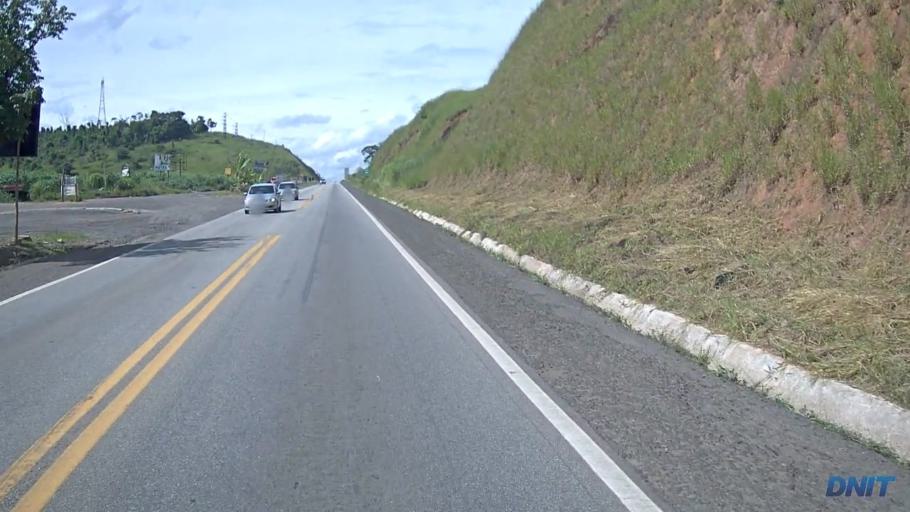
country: BR
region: Minas Gerais
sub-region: Ipatinga
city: Ipatinga
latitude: -19.4201
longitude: -42.4941
